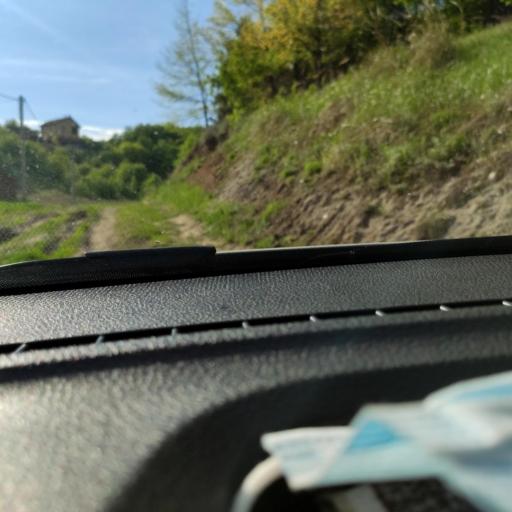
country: RU
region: Voronezj
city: Ramon'
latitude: 51.9395
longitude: 39.3710
